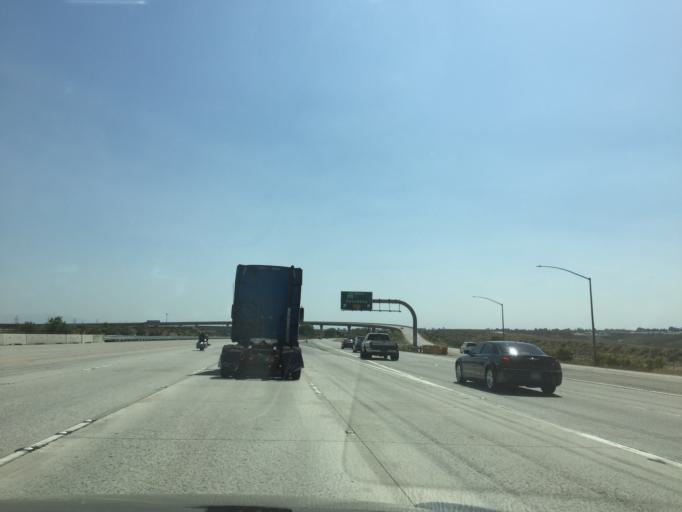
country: US
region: California
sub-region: San Bernardino County
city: Fontana
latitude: 34.1418
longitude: -117.4897
